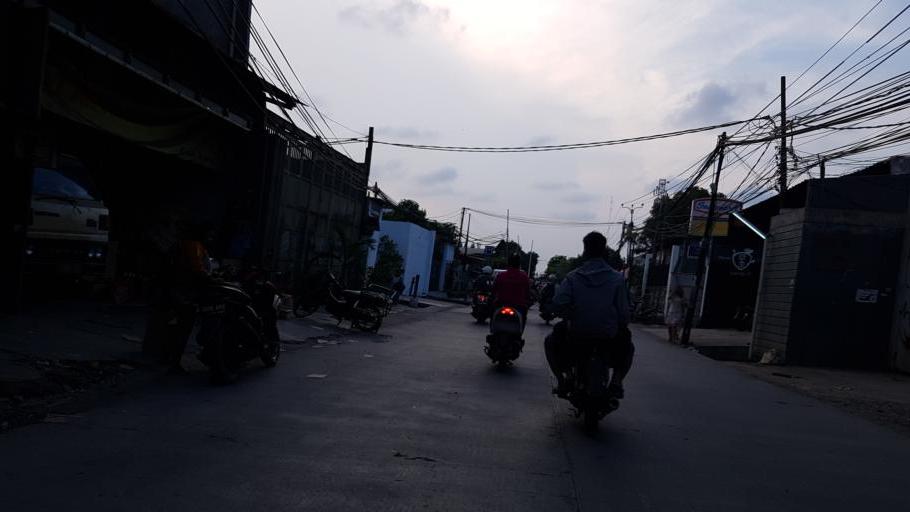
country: ID
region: Jakarta Raya
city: Jakarta
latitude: -6.1407
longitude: 106.7682
